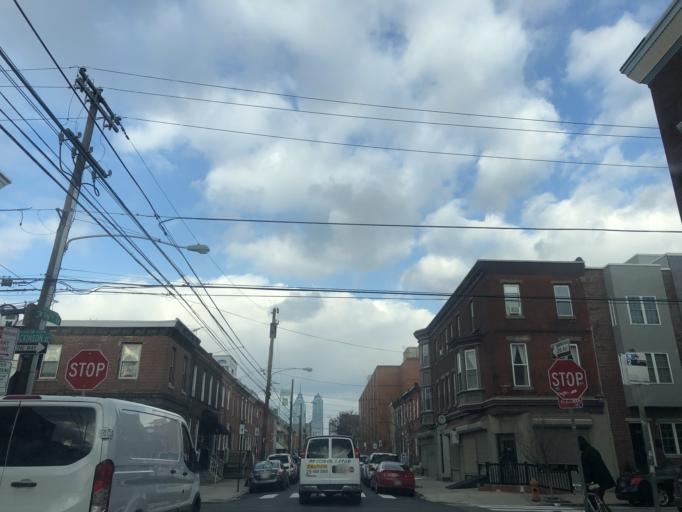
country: US
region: Pennsylvania
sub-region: Philadelphia County
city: Philadelphia
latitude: 39.9320
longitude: -75.1714
